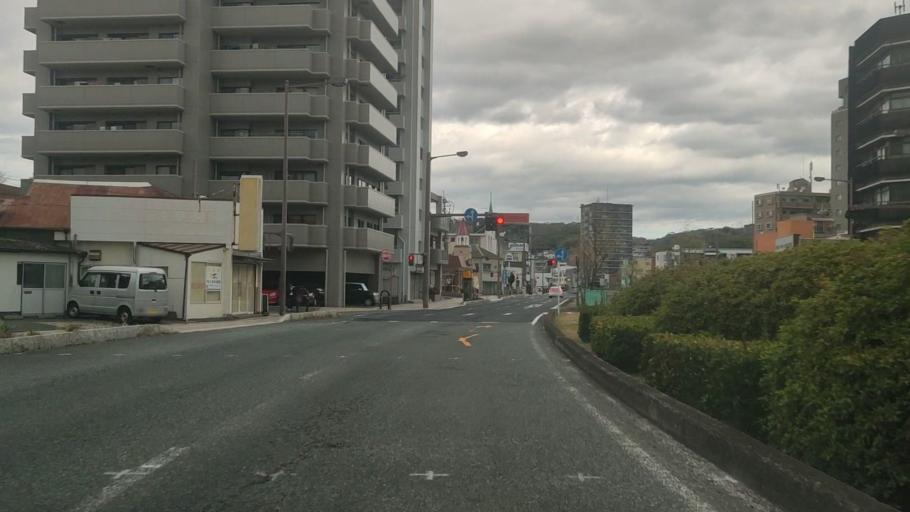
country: JP
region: Yamaguchi
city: Shimonoseki
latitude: 33.9613
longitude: 130.9416
